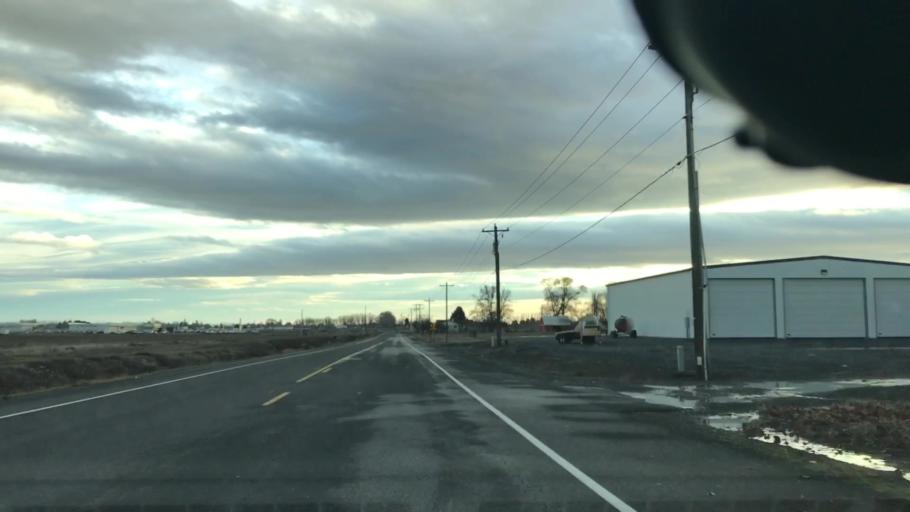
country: US
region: Washington
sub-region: Grant County
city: Moses Lake
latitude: 47.1048
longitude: -119.2361
